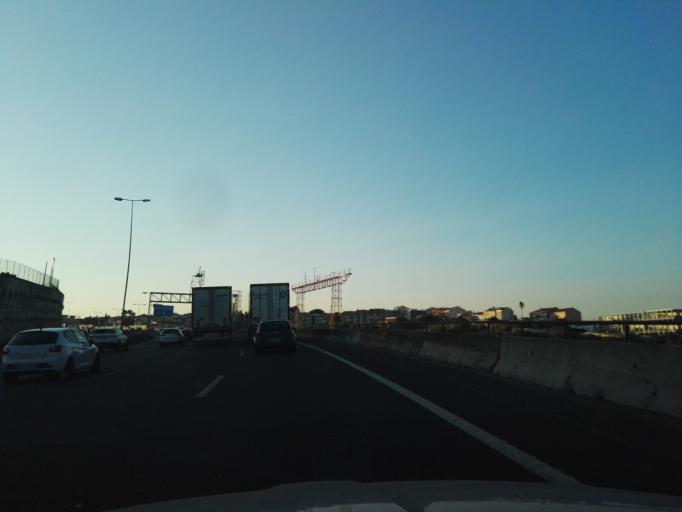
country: PT
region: Lisbon
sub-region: Loures
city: Camarate
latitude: 38.7989
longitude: -9.1249
